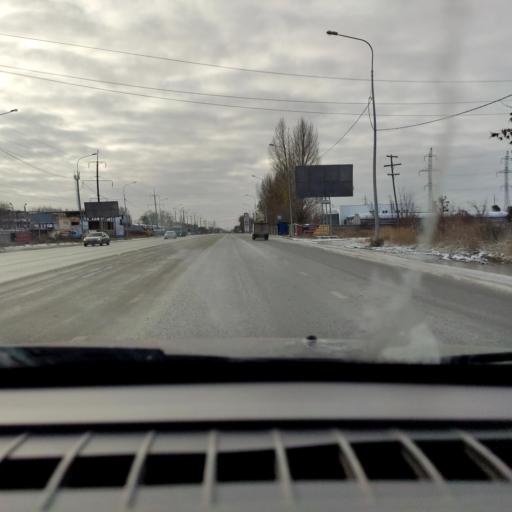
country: RU
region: Samara
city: Tol'yatti
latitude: 53.5771
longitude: 49.2935
